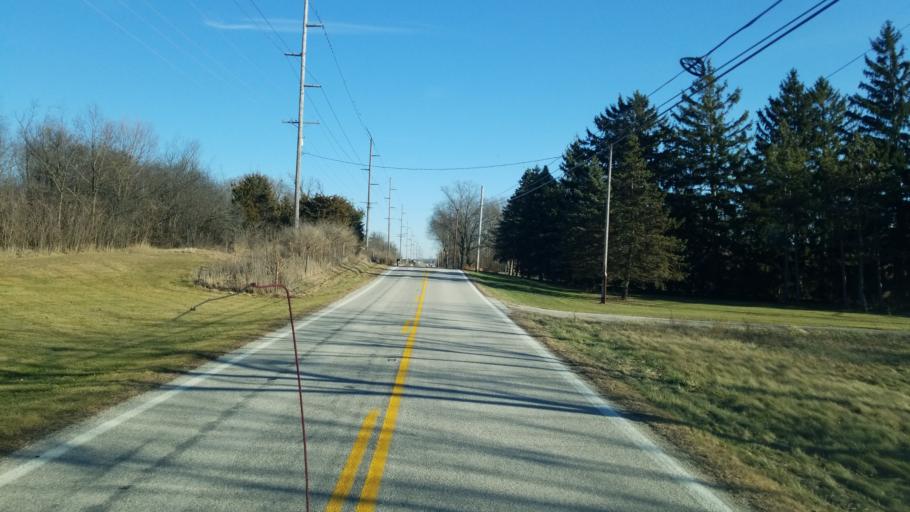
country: US
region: Ohio
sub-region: Wood County
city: Pemberville
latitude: 41.4500
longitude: -83.4264
